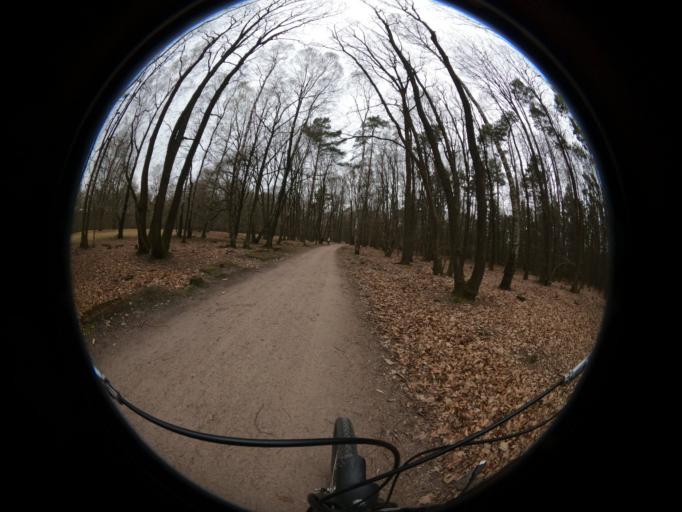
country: DE
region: Lower Saxony
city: Neu Wulmstorf
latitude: 53.4465
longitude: 9.8530
